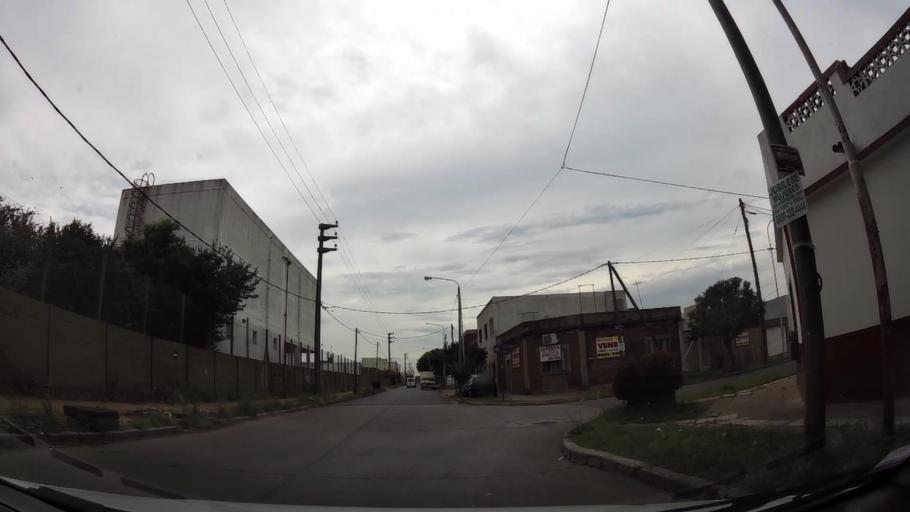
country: AR
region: Buenos Aires
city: San Justo
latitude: -34.6785
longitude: -58.5211
